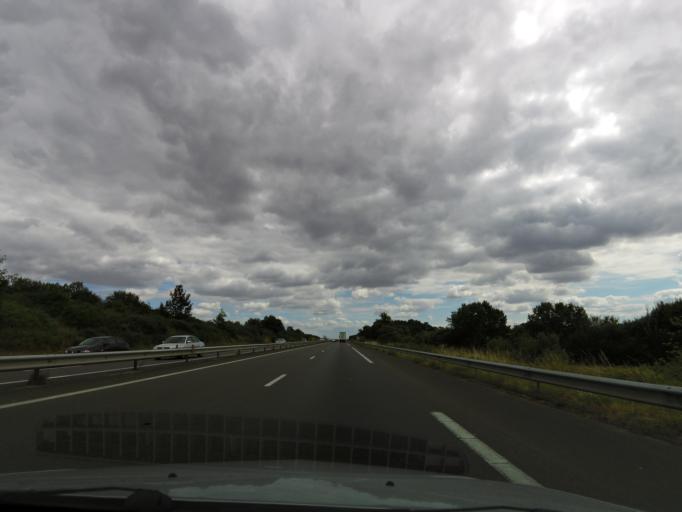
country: FR
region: Pays de la Loire
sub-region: Departement de la Loire-Atlantique
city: Le Bignon
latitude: 47.0929
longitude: -1.4629
